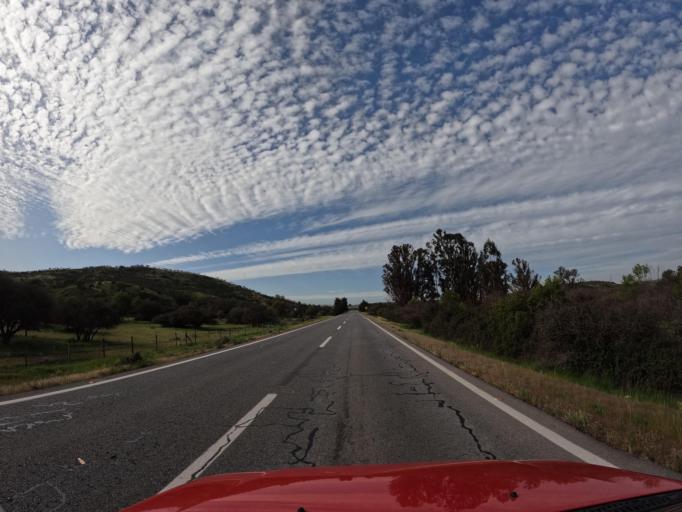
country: CL
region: O'Higgins
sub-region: Provincia de Colchagua
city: Santa Cruz
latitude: -34.2931
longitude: -71.7308
